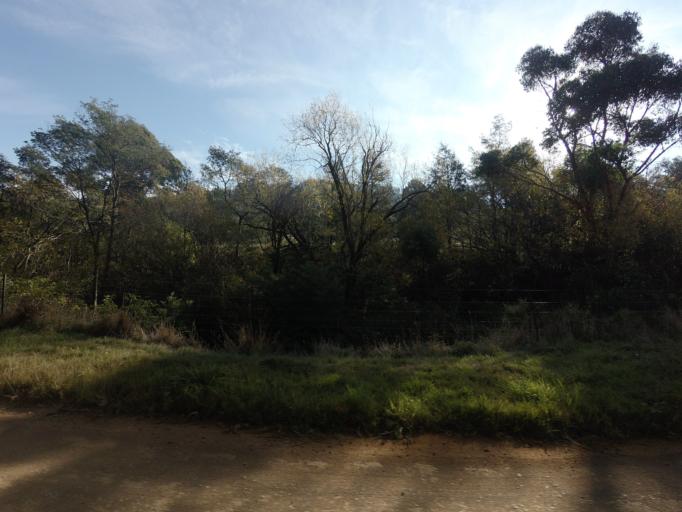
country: AU
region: Tasmania
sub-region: Sorell
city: Sorell
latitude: -42.4955
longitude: 147.4335
